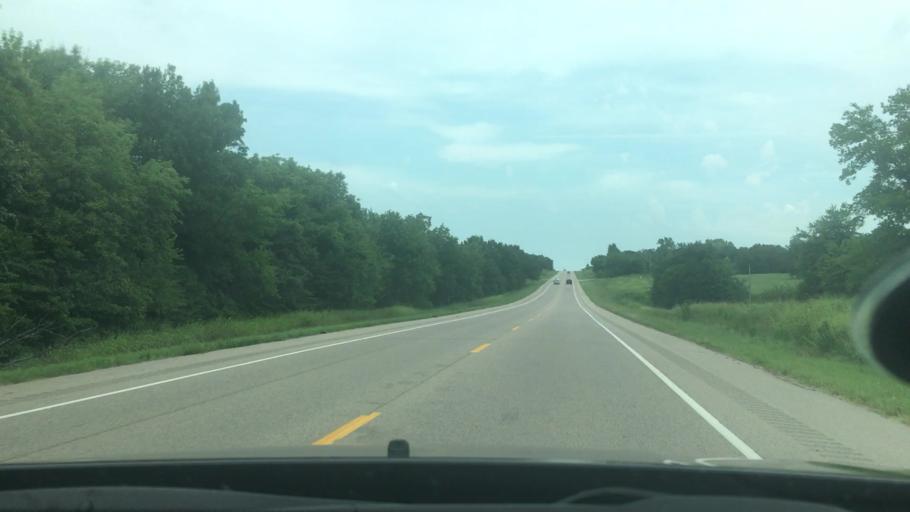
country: US
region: Oklahoma
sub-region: Seminole County
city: Konawa
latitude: 35.0065
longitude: -96.6787
